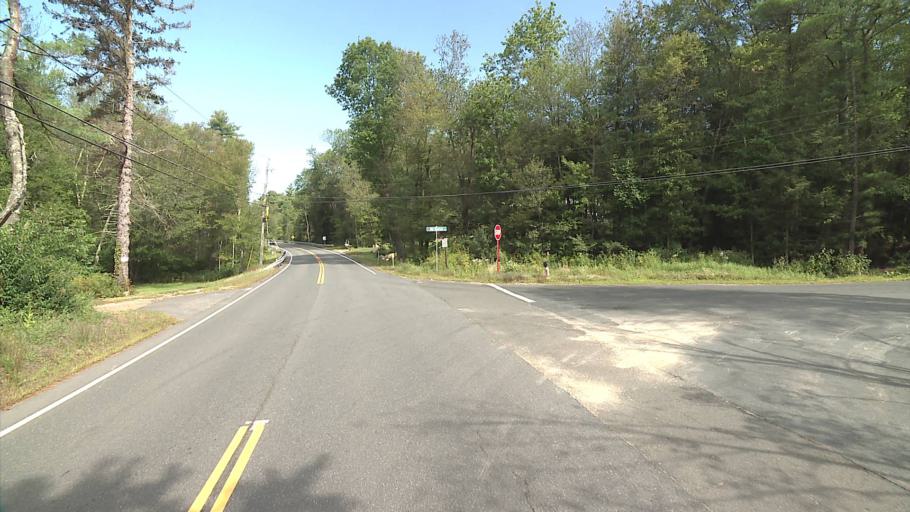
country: US
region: Connecticut
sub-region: Tolland County
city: Stafford
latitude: 42.0134
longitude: -72.3160
